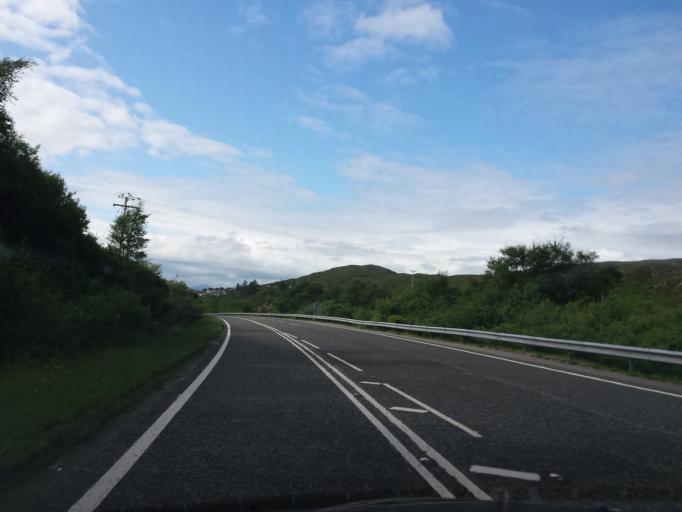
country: GB
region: Scotland
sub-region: Argyll and Bute
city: Isle Of Mull
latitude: 56.9888
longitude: -5.8255
